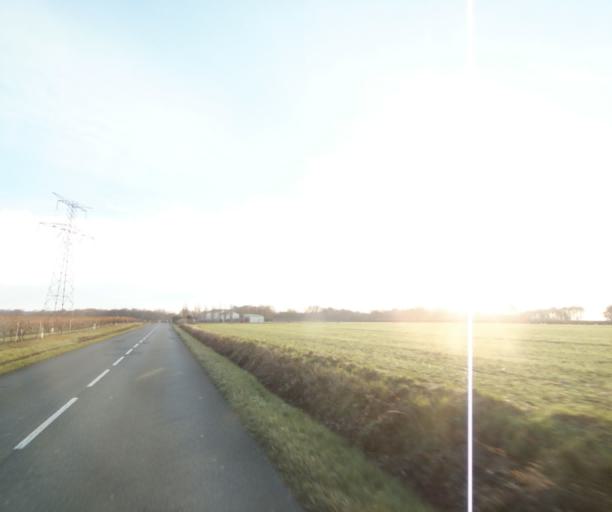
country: FR
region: Poitou-Charentes
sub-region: Departement de la Charente-Maritime
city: Fontcouverte
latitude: 45.7767
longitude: -0.5559
